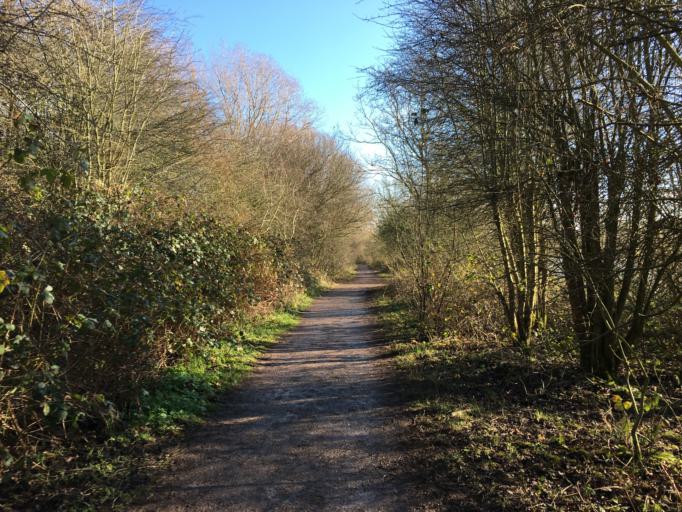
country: GB
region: England
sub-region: Nottinghamshire
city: Gotham
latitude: 52.9077
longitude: -1.2181
